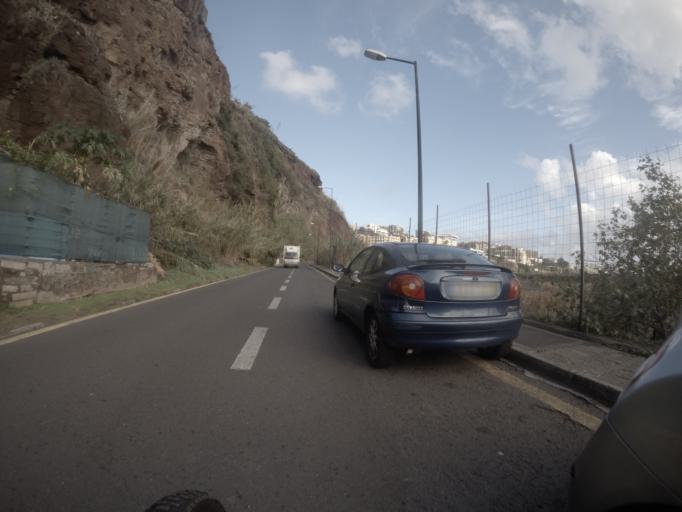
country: PT
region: Madeira
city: Camara de Lobos
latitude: 32.6428
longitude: -16.9544
